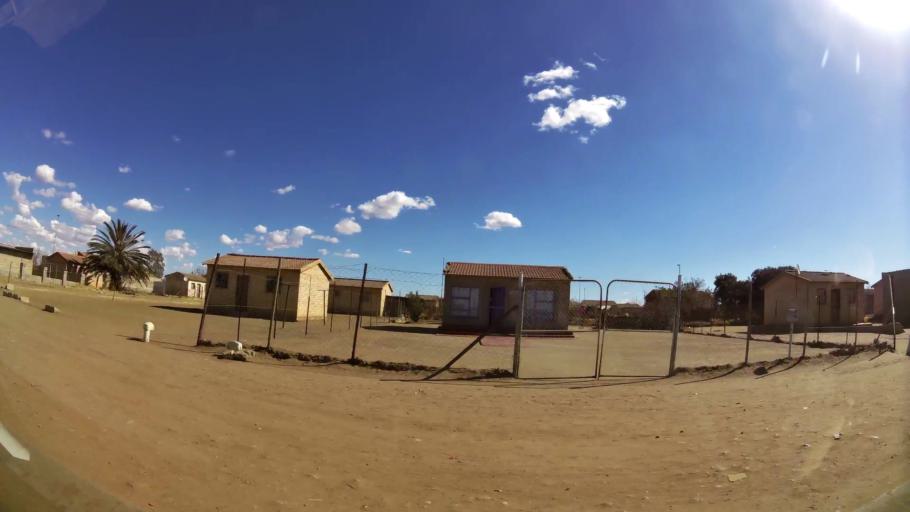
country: ZA
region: North-West
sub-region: Dr Kenneth Kaunda District Municipality
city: Klerksdorp
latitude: -26.8711
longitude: 26.5749
